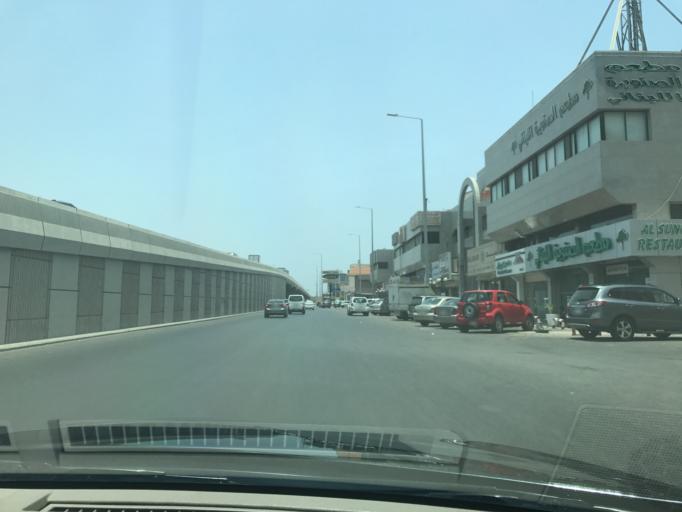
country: SA
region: Makkah
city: Jeddah
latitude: 21.5758
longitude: 39.1463
